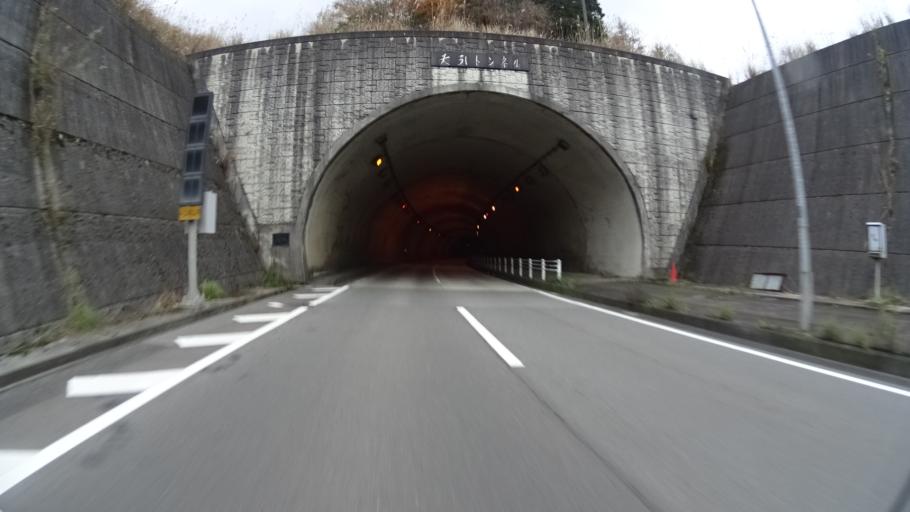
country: JP
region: Hyogo
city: Sasayama
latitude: 35.0732
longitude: 135.3810
